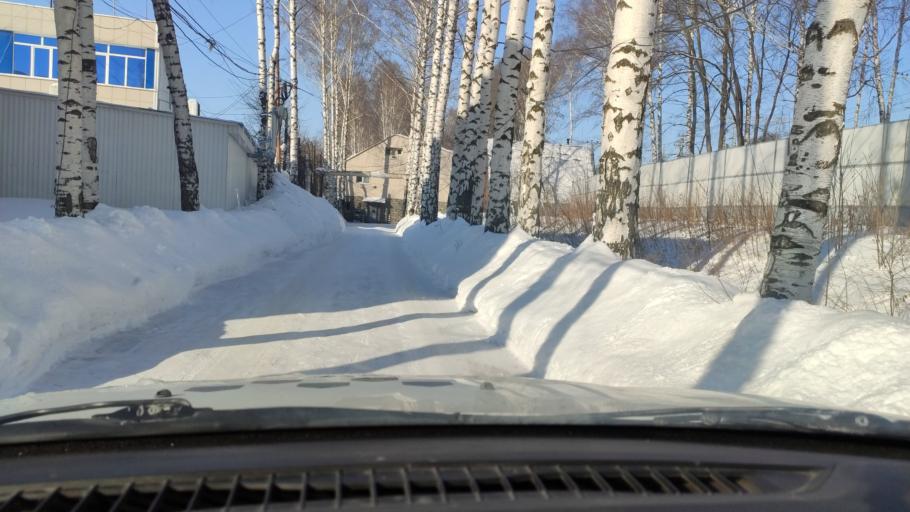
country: RU
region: Perm
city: Froly
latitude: 57.9420
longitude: 56.2676
